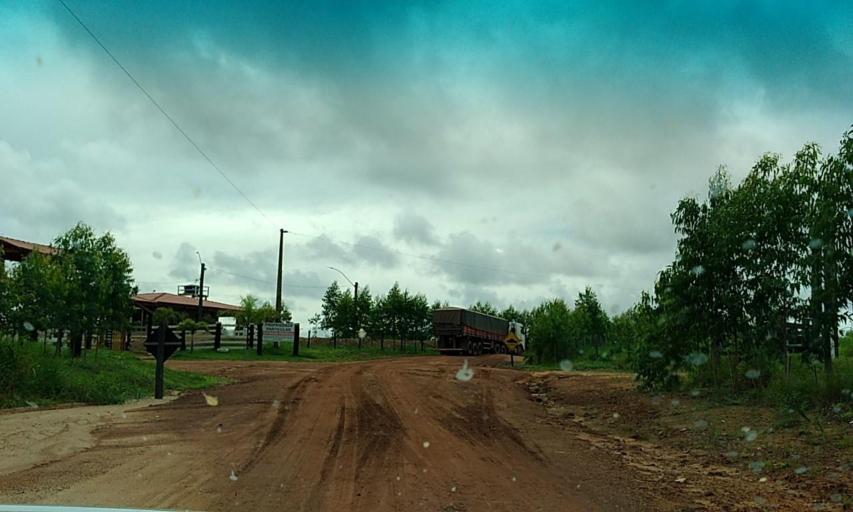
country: BR
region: Para
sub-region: Altamira
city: Altamira
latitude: -3.0614
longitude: -51.7215
